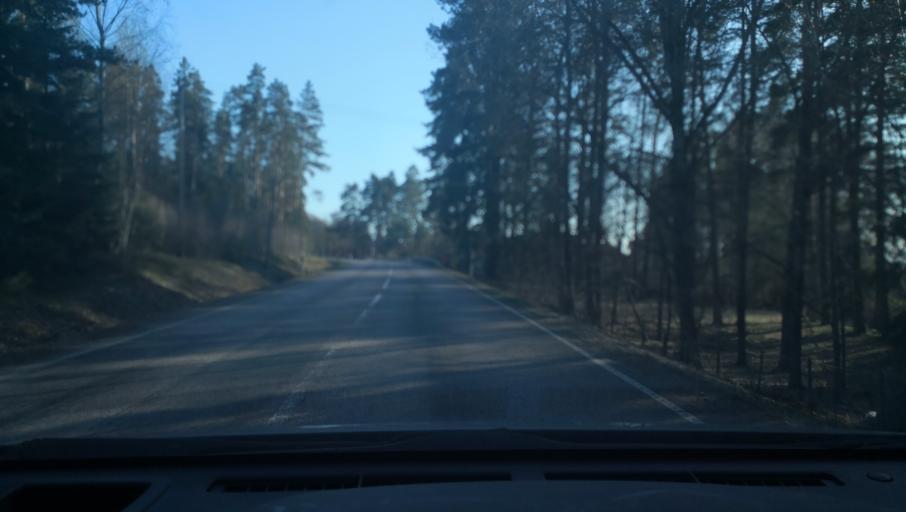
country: SE
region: Uppsala
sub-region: Heby Kommun
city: Heby
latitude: 60.0014
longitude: 16.8334
